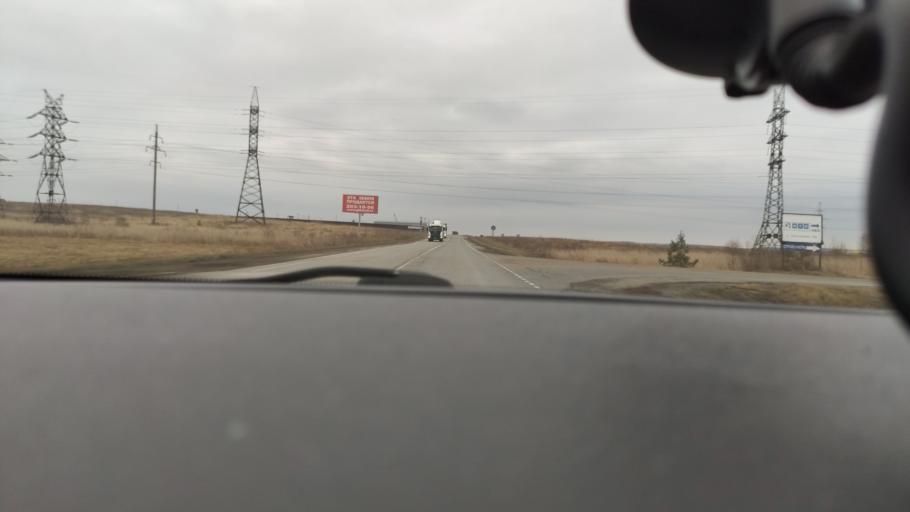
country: RU
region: Perm
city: Froly
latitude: 57.9193
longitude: 56.1815
